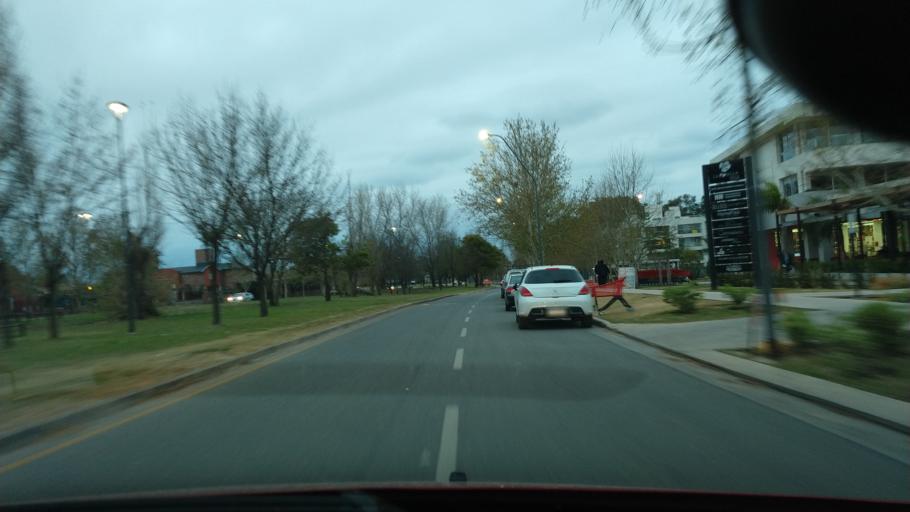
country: AR
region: Cordoba
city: La Calera
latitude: -31.3717
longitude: -64.2772
